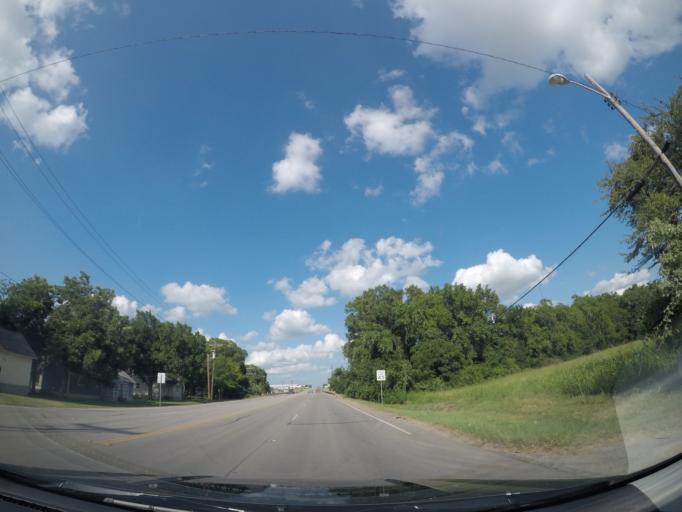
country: US
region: Texas
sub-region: Lavaca County
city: Hallettsville
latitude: 29.4454
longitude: -96.9329
